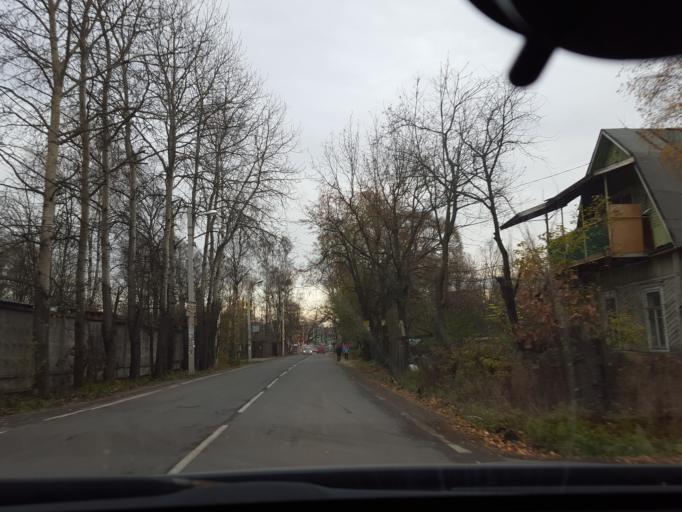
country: RU
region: St.-Petersburg
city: Shuvalovo
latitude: 60.0437
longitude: 30.2975
